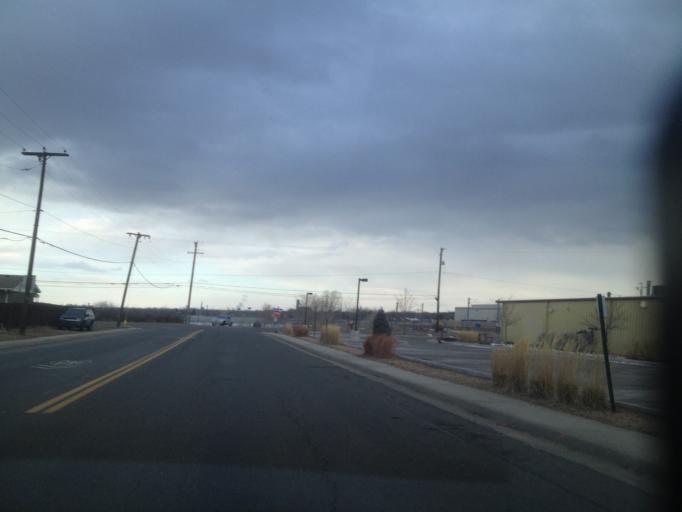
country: US
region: Colorado
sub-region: Adams County
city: Berkley
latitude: 39.8055
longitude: -105.0452
